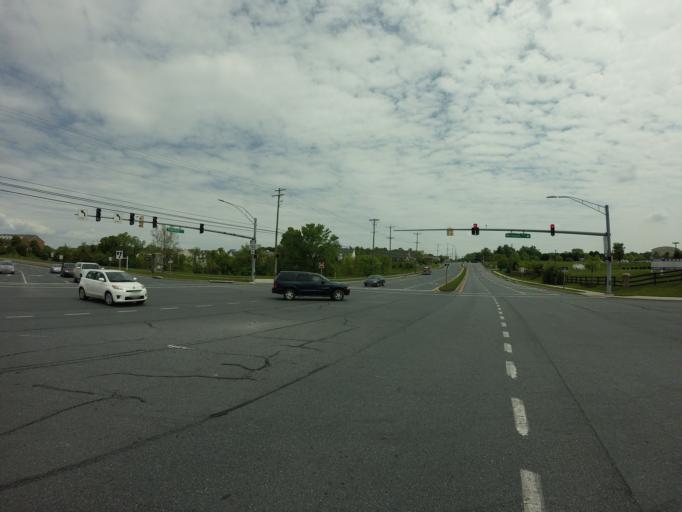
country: US
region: Maryland
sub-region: Frederick County
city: Urbana
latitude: 39.3273
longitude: -77.3444
